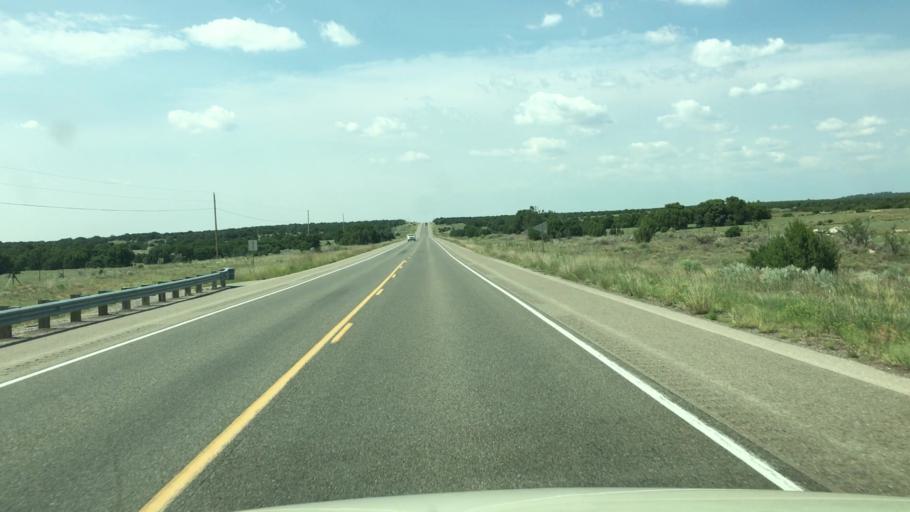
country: US
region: New Mexico
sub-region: Torrance County
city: Moriarty
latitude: 35.0479
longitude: -105.6863
